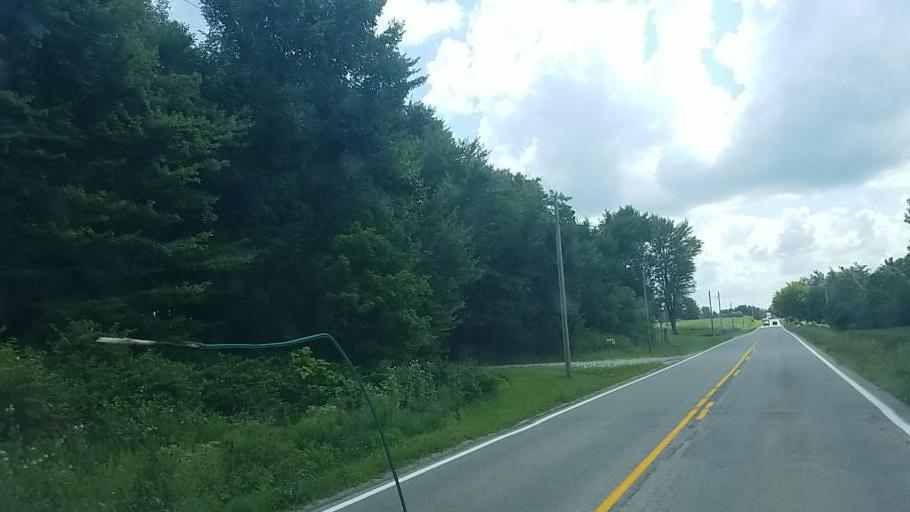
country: US
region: Ohio
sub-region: Morrow County
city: Mount Gilead
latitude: 40.4730
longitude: -82.8212
